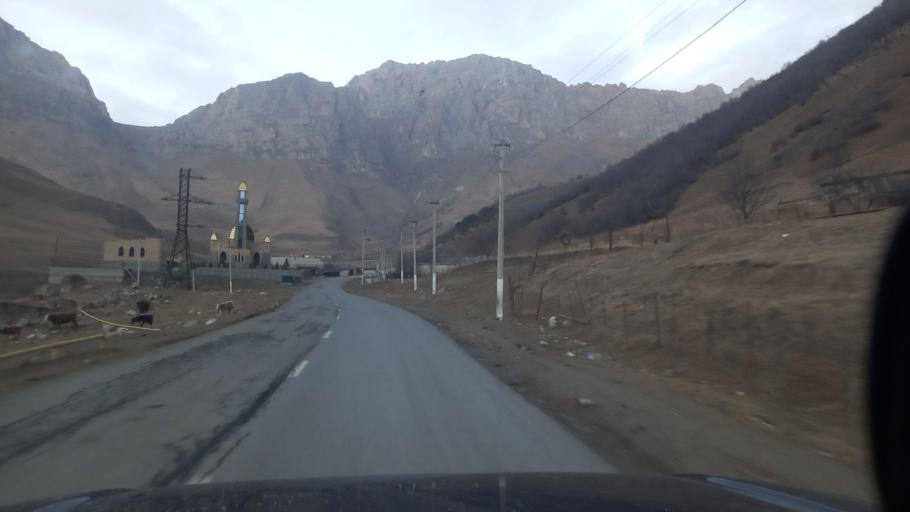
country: RU
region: Ingushetiya
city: Dzhayrakh
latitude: 42.8139
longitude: 44.8129
